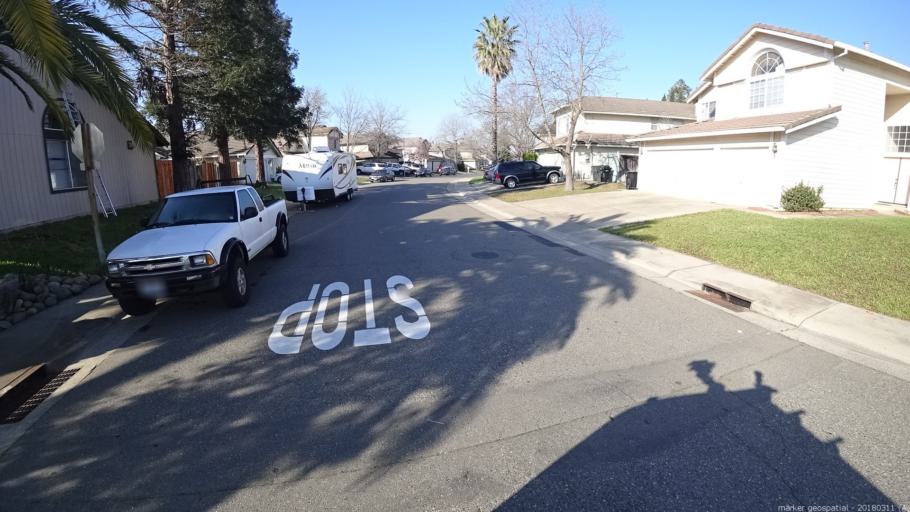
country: US
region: California
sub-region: Sacramento County
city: Vineyard
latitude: 38.4568
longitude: -121.3846
